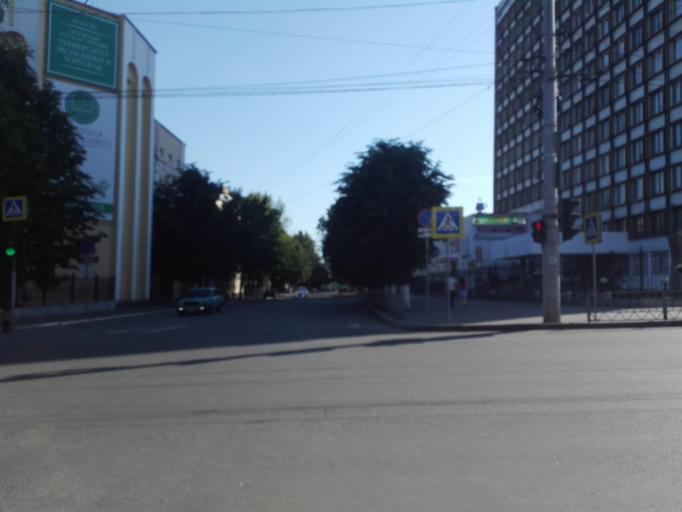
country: RU
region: Orjol
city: Orel
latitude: 52.9703
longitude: 36.0556
